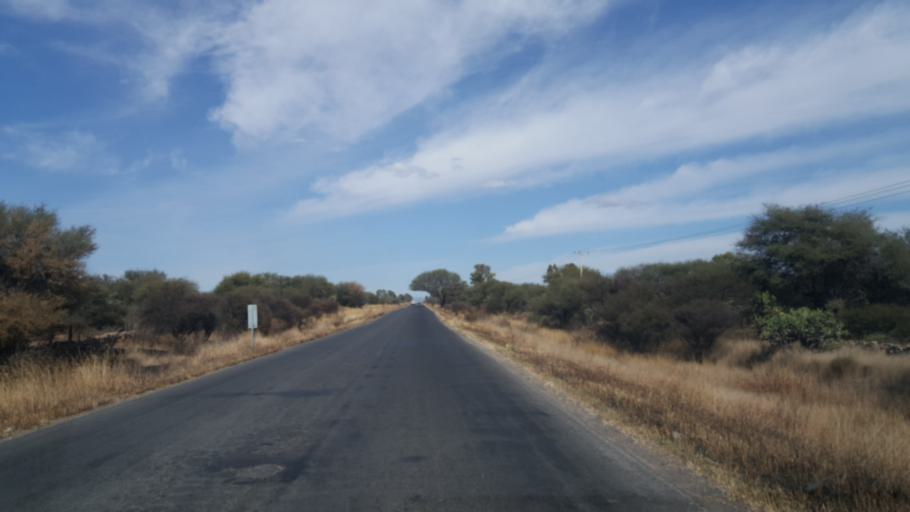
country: MX
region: Jalisco
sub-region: Lagos de Moreno
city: Geovillas Laureles del Campanario
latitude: 21.2794
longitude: -101.9373
